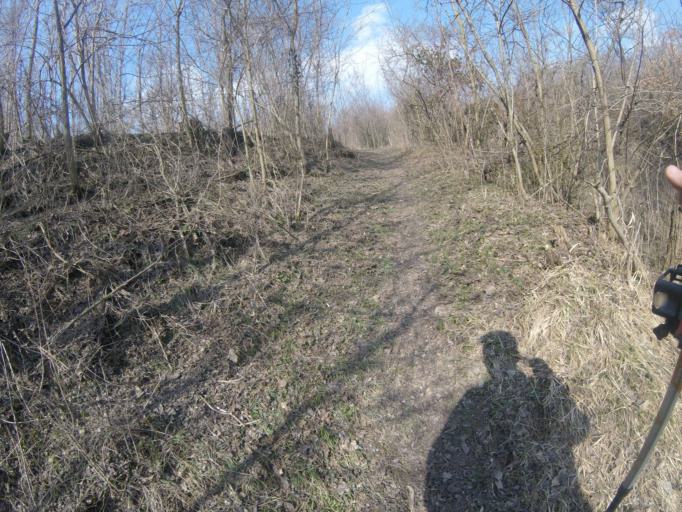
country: HU
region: Komarom-Esztergom
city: Nyergesujfalu
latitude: 47.7318
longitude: 18.5568
